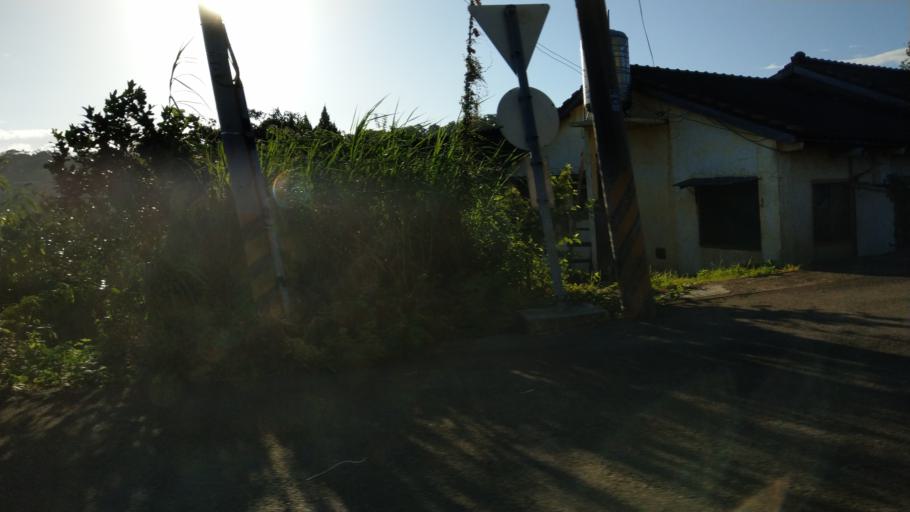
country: TW
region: Taiwan
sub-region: Miaoli
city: Miaoli
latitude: 24.5403
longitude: 120.7964
